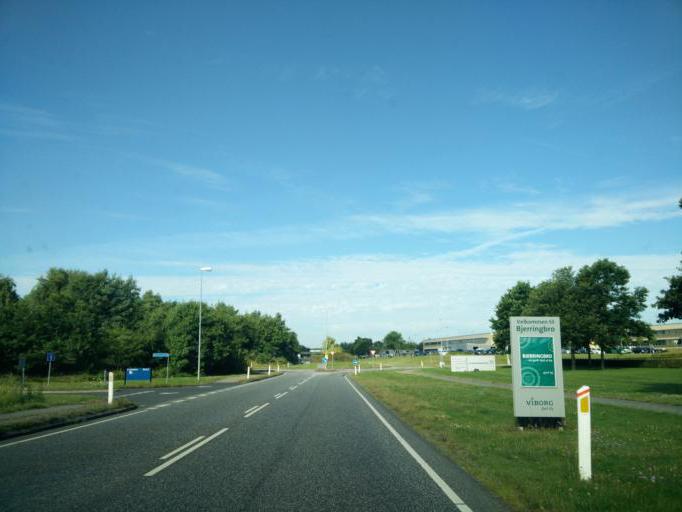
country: DK
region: Central Jutland
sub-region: Viborg Kommune
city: Bjerringbro
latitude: 56.3814
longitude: 9.6823
